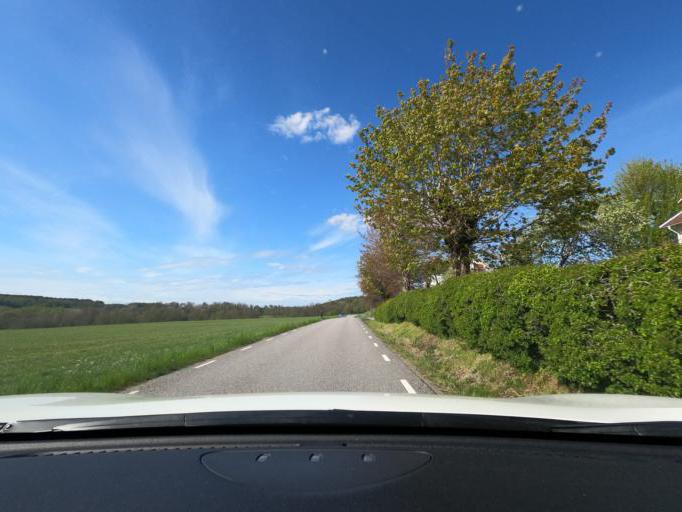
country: SE
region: Vaestra Goetaland
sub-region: Harryda Kommun
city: Ravlanda
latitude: 57.6222
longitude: 12.4973
